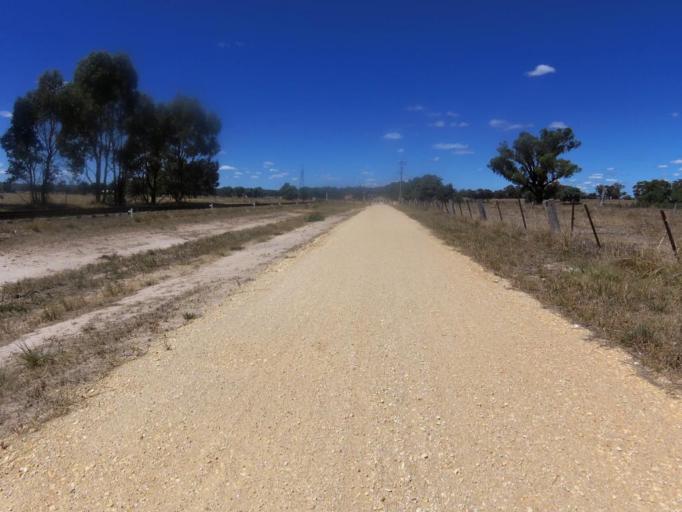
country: AU
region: Victoria
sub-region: Mount Alexander
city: Castlemaine
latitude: -37.0197
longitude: 144.1465
